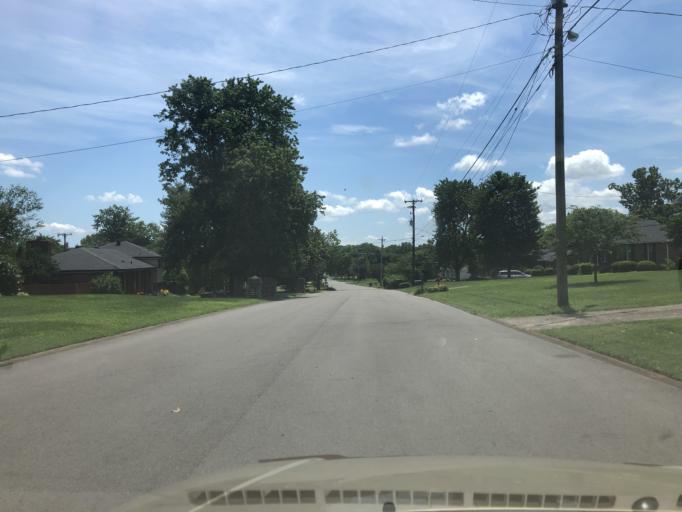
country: US
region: Tennessee
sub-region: Davidson County
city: Lakewood
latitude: 36.2453
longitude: -86.6728
